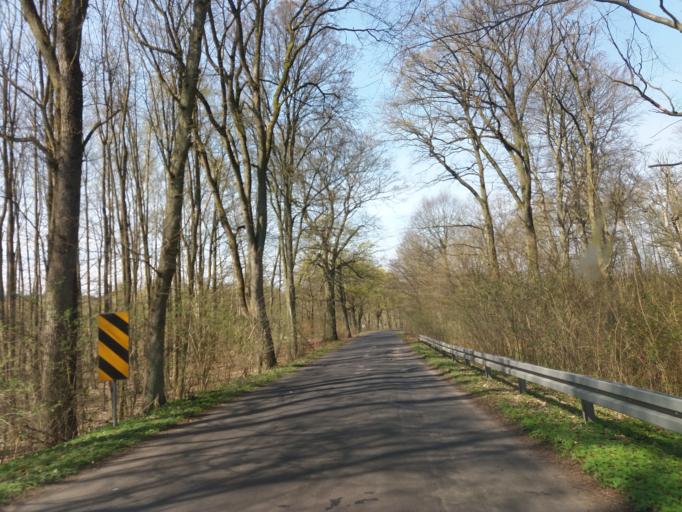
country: PL
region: West Pomeranian Voivodeship
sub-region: Powiat choszczenski
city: Recz
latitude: 53.1921
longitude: 15.6380
